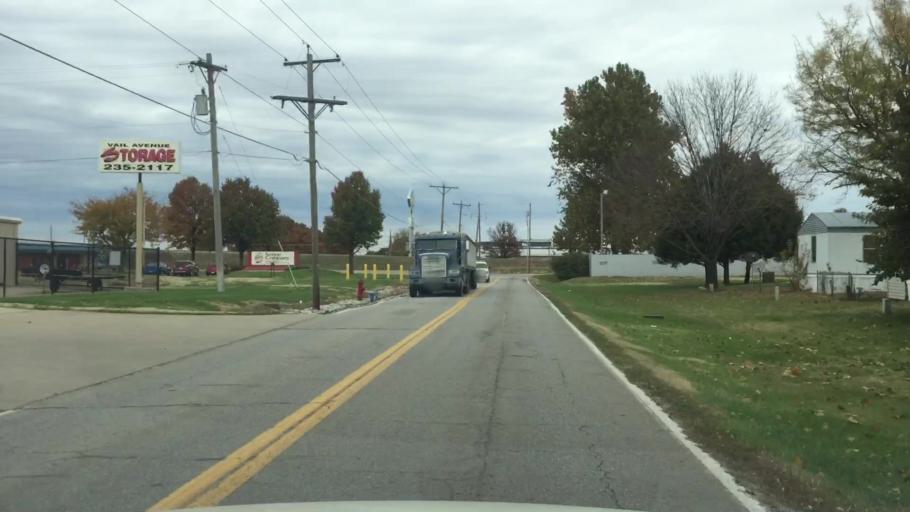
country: US
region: Kansas
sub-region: Shawnee County
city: Topeka
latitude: 39.0889
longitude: -95.6943
